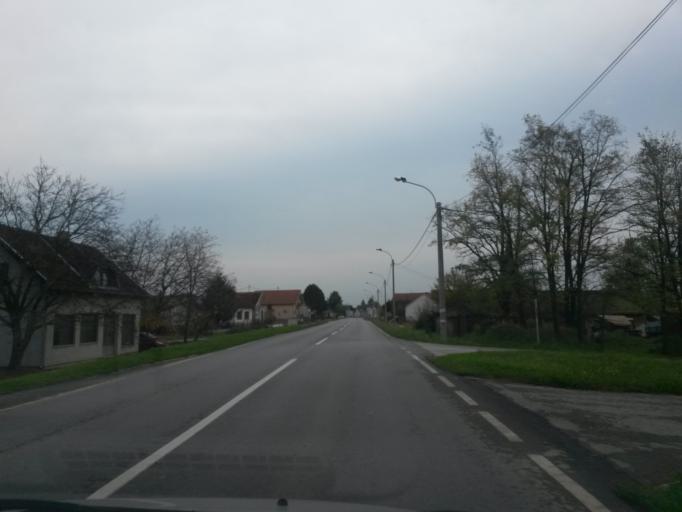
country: HR
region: Osjecko-Baranjska
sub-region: Grad Osijek
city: Bilje
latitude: 45.6100
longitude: 18.7389
